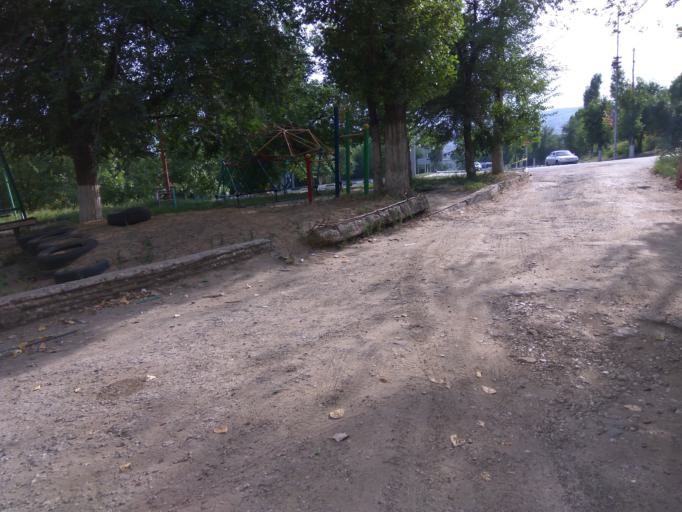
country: RU
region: Saratov
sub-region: Saratovskiy Rayon
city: Saratov
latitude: 51.5508
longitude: 46.0528
